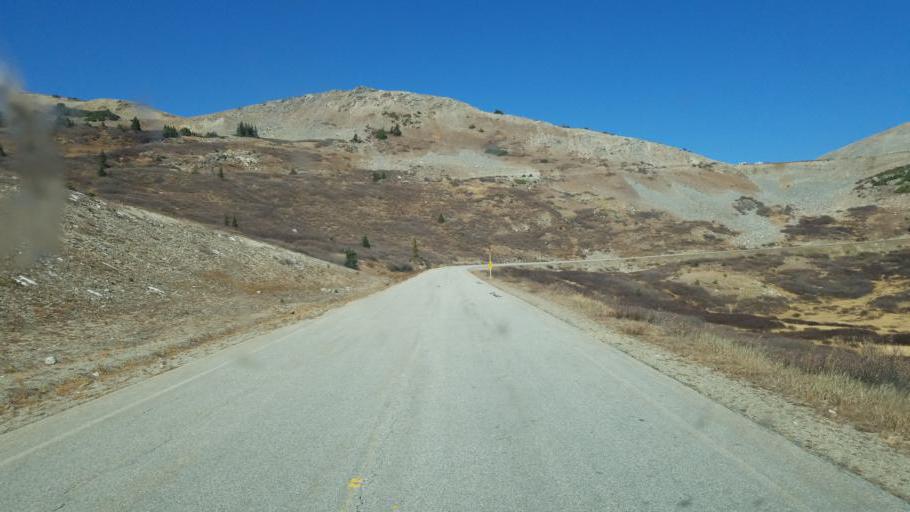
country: US
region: Colorado
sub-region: Chaffee County
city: Buena Vista
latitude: 38.8234
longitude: -106.4068
